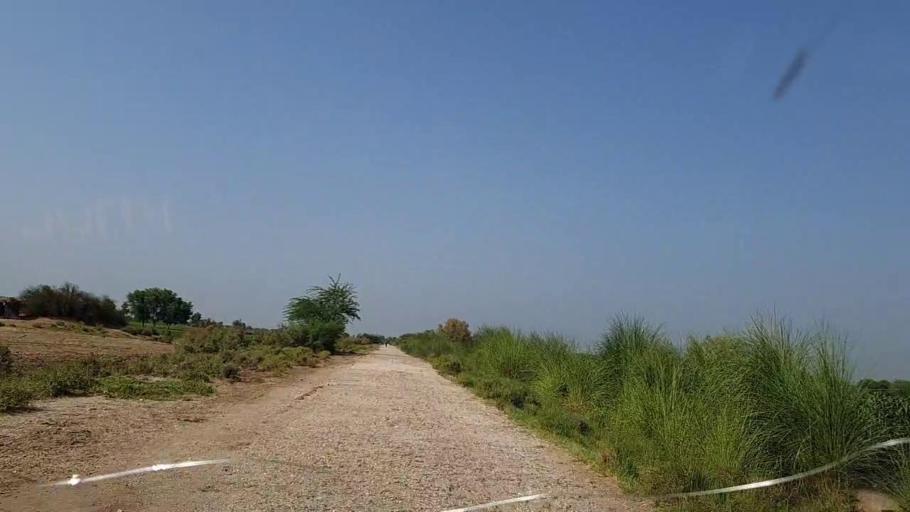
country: PK
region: Sindh
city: Khanpur
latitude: 27.7091
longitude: 69.3893
